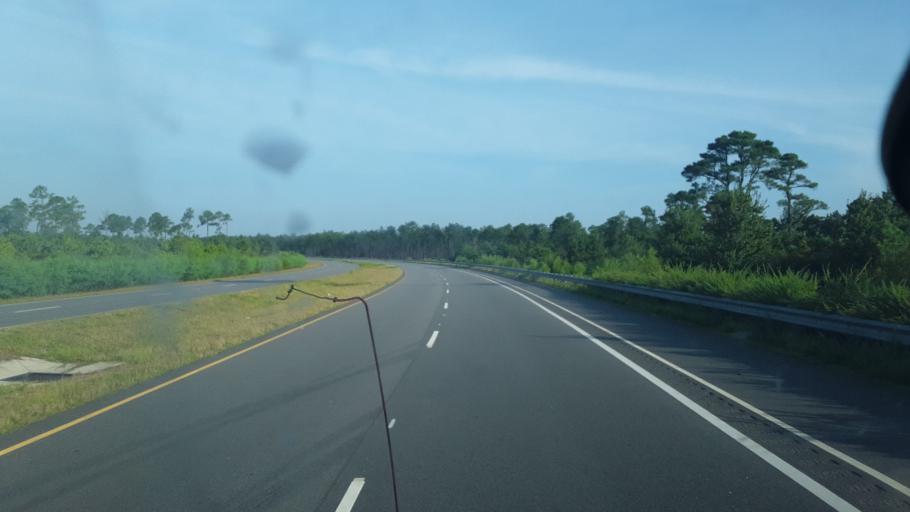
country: US
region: South Carolina
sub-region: Horry County
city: Forestbrook
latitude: 33.8006
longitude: -78.8838
